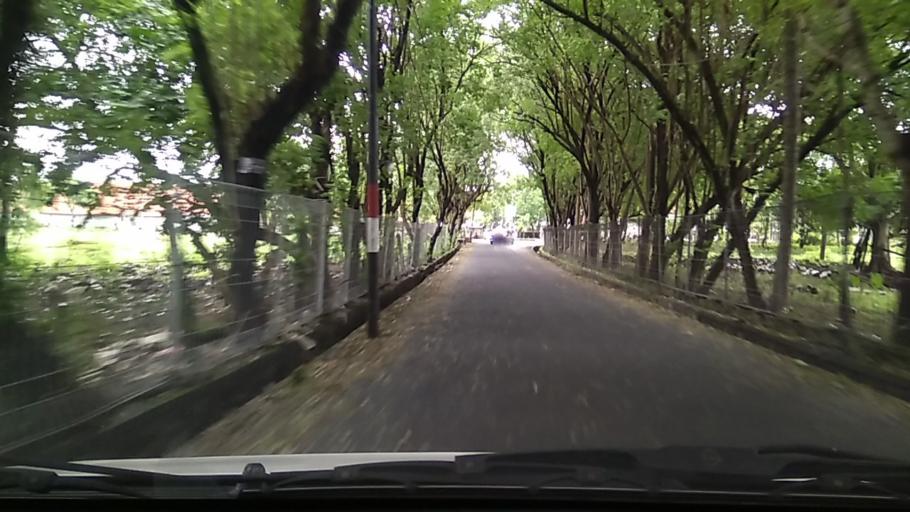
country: ID
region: Bali
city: Kelanabian
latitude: -8.7673
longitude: 115.1705
